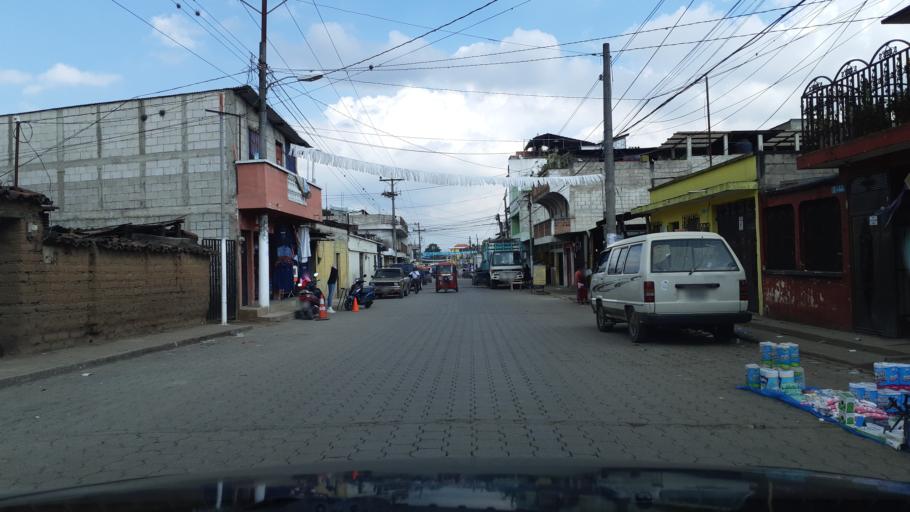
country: GT
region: Chimaltenango
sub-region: Municipio de Chimaltenango
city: Chimaltenango
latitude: 14.6664
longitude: -90.8148
